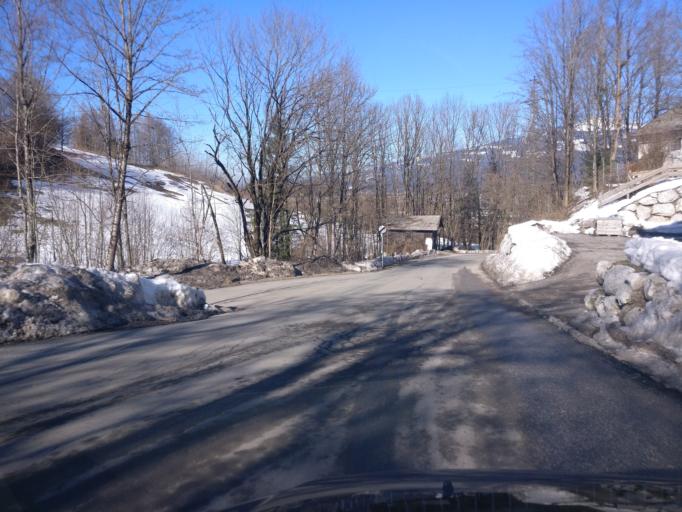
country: AT
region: Salzburg
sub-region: Politischer Bezirk Hallein
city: Kuchl
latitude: 47.6109
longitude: 13.1405
